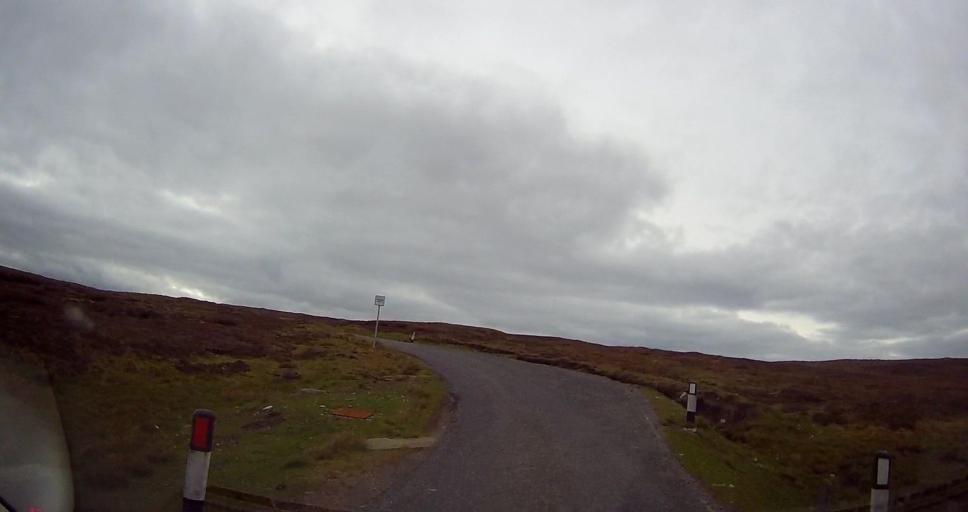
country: GB
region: Scotland
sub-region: Shetland Islands
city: Shetland
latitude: 60.5120
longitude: -1.1159
